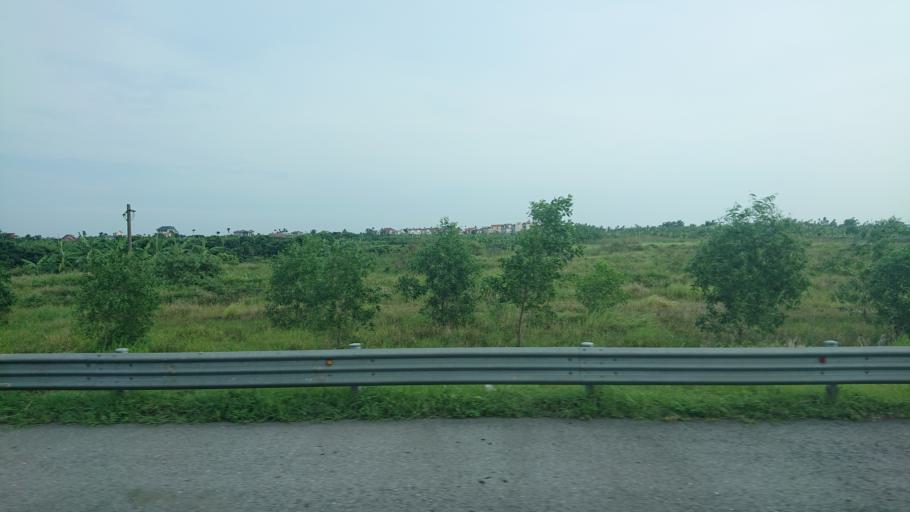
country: VN
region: Hai Phong
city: An Lao
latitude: 20.8151
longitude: 106.4933
